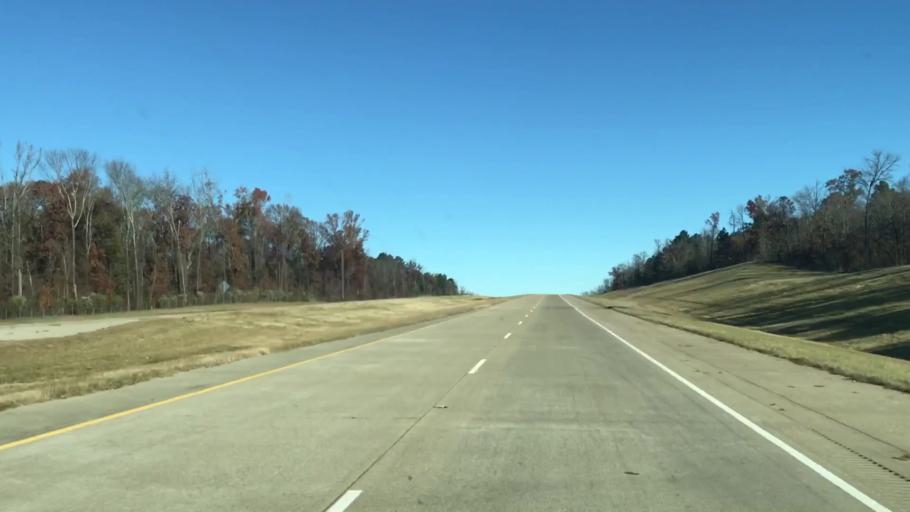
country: US
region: Louisiana
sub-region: Caddo Parish
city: Oil City
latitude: 32.7892
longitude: -93.8879
